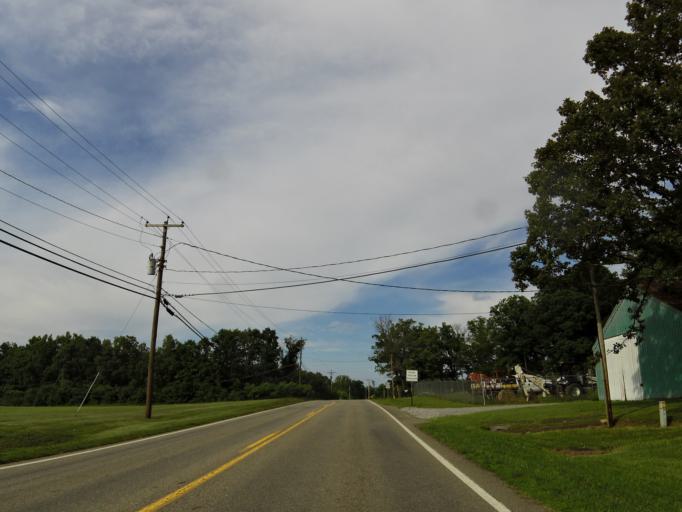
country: US
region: Tennessee
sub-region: Blount County
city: Eagleton Village
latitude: 35.8652
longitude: -83.9625
